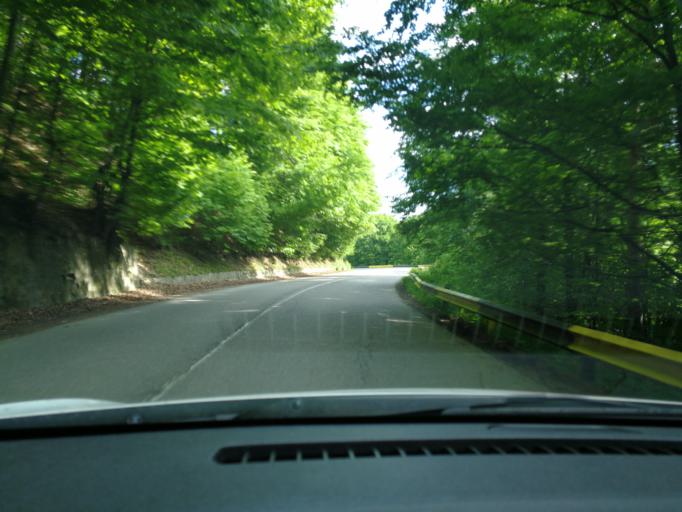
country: RO
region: Prahova
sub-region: Comuna Valea Doftanei
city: Tesila
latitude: 45.2617
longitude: 25.7347
